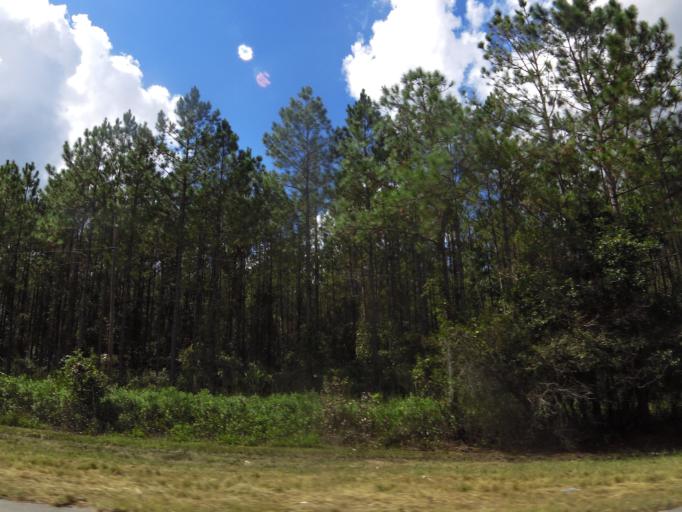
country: US
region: Georgia
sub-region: Charlton County
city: Folkston
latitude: 30.9369
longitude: -82.0222
